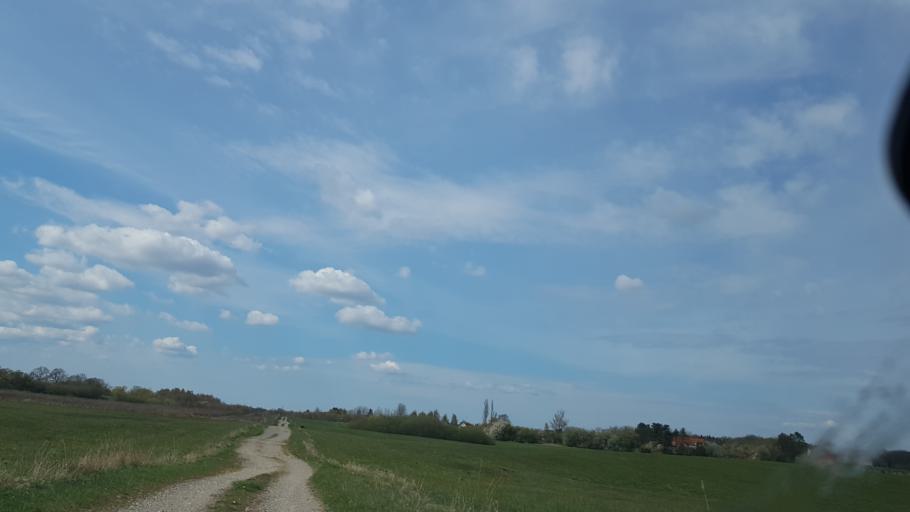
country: DK
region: Capital Region
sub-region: Allerod Kommune
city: Lillerod
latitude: 55.8954
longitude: 12.3375
